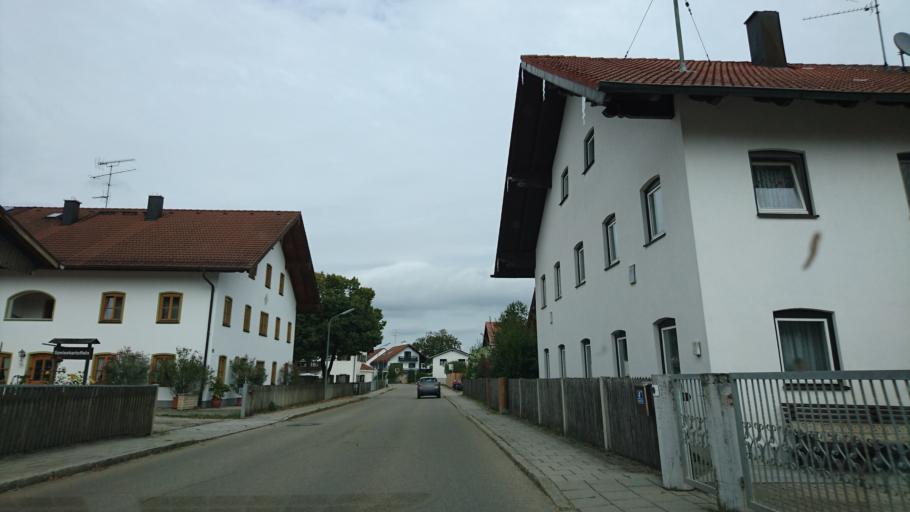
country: DE
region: Bavaria
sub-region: Upper Bavaria
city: Vaterstetten
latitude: 48.1149
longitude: 11.7968
